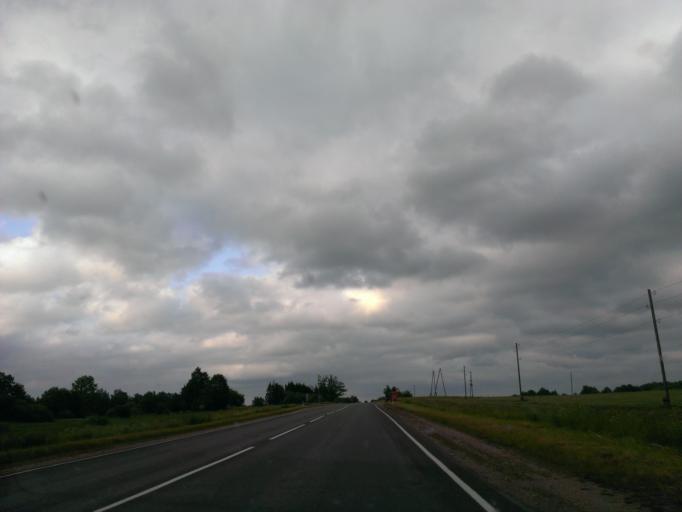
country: LV
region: Skrunda
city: Skrunda
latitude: 56.6768
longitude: 22.1614
